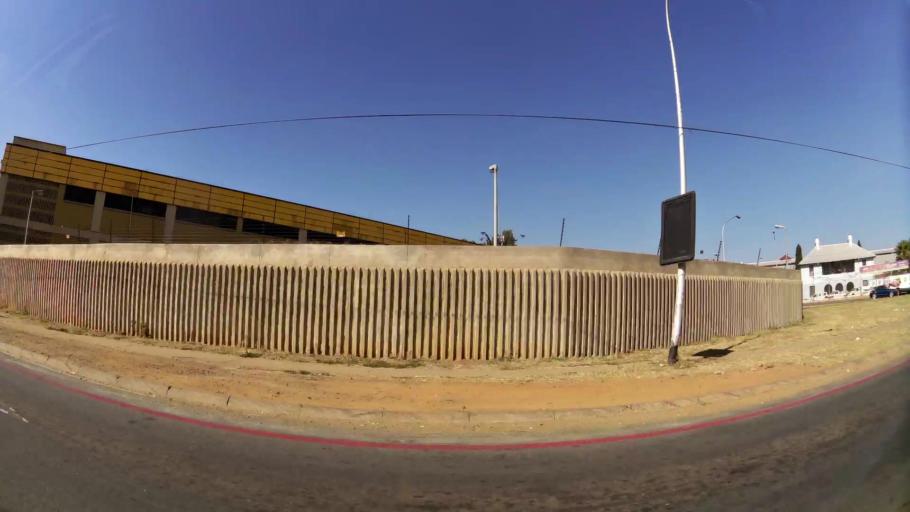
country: ZA
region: Gauteng
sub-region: City of Tshwane Metropolitan Municipality
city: Pretoria
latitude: -25.7526
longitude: 28.1752
